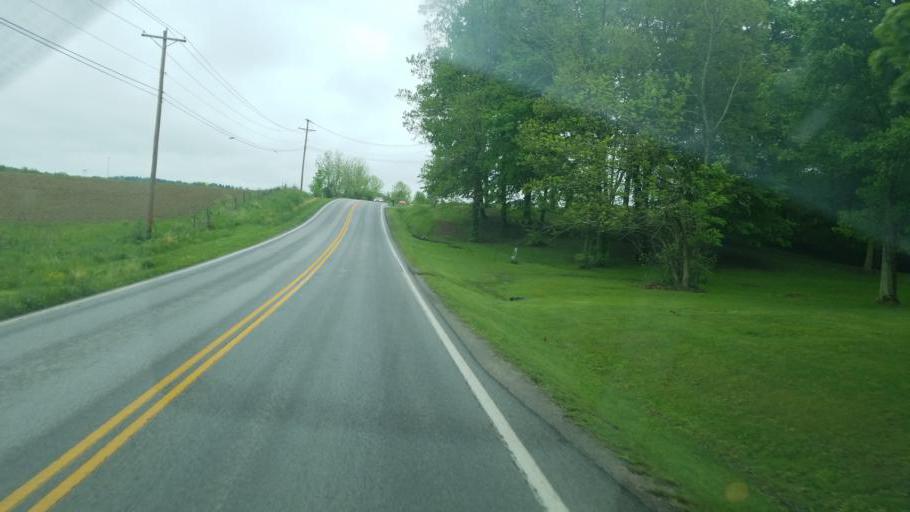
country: US
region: Ohio
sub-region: Highland County
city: Hillsboro
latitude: 39.2220
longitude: -83.6210
